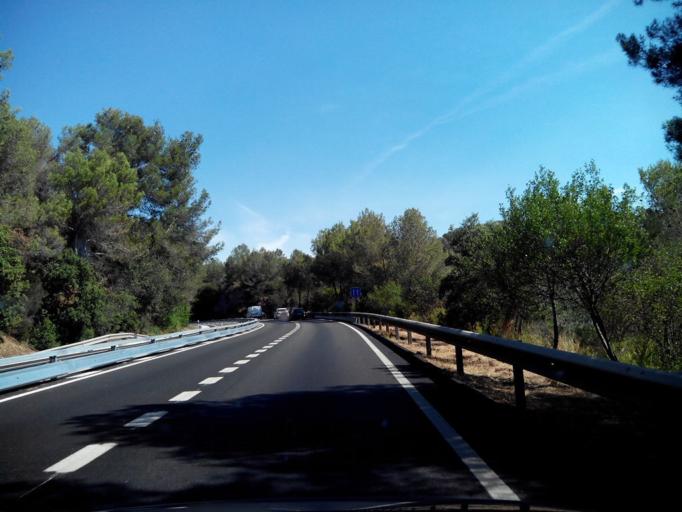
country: ES
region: Catalonia
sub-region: Provincia de Barcelona
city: Viladecavalls
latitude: 41.5726
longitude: 1.9633
